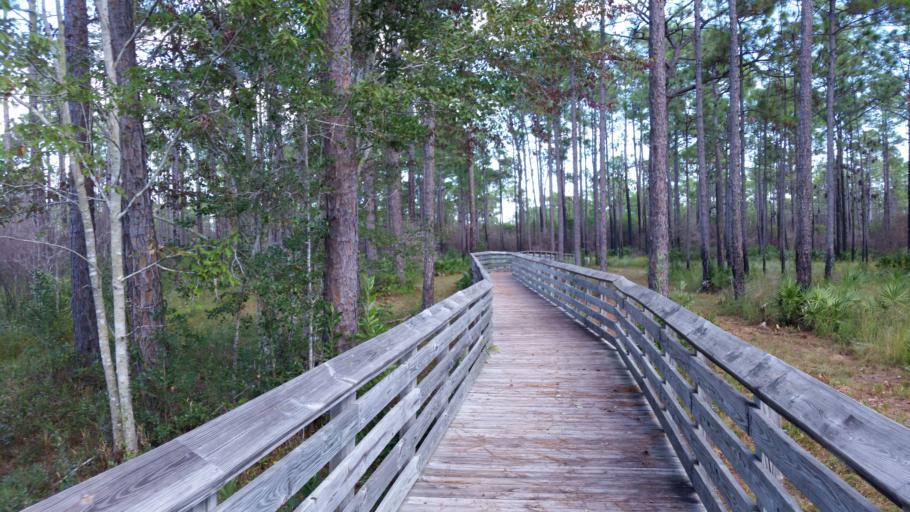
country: US
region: Florida
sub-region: Escambia County
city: Myrtle Grove
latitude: 30.3684
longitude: -87.4067
